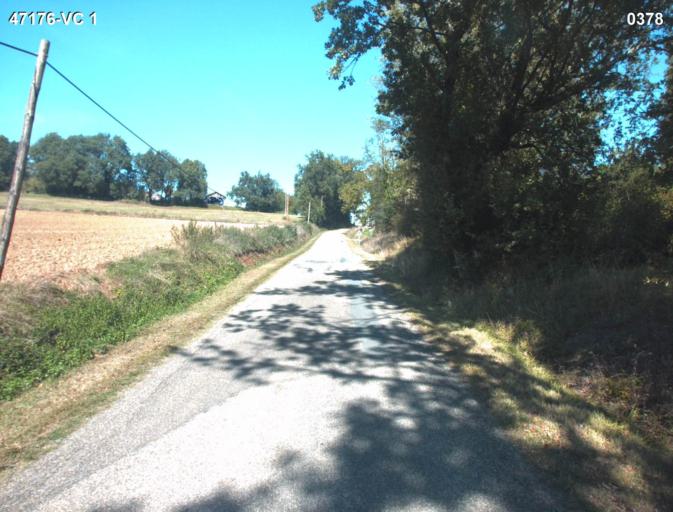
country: FR
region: Aquitaine
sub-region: Departement du Lot-et-Garonne
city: Lavardac
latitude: 44.1960
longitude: 0.2925
